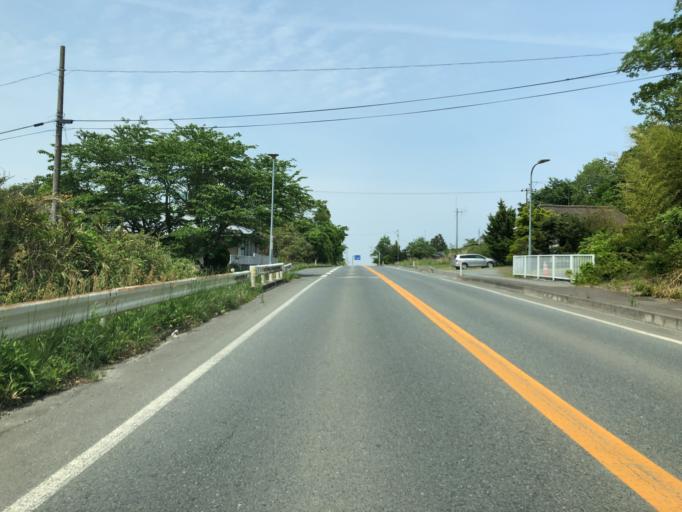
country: JP
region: Miyagi
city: Marumori
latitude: 37.8520
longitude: 140.9202
